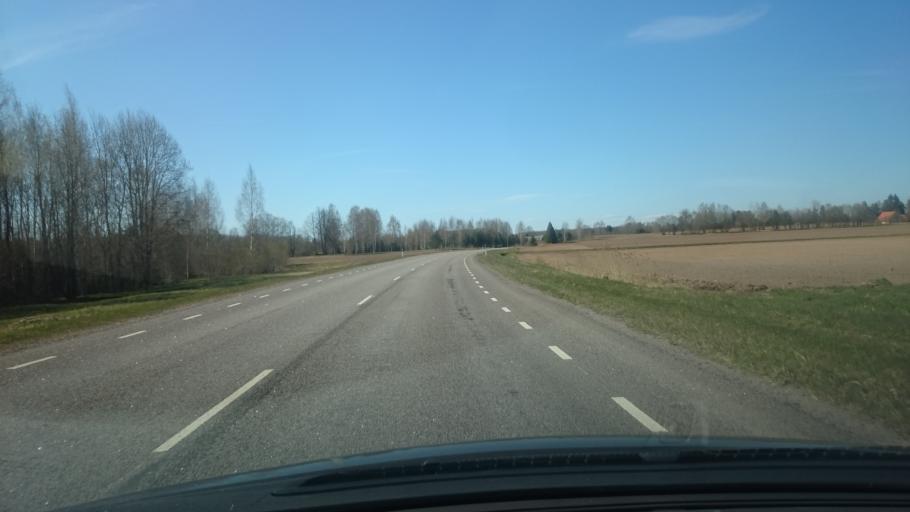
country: EE
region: Polvamaa
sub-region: Polva linn
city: Polva
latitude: 58.2452
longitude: 27.0055
